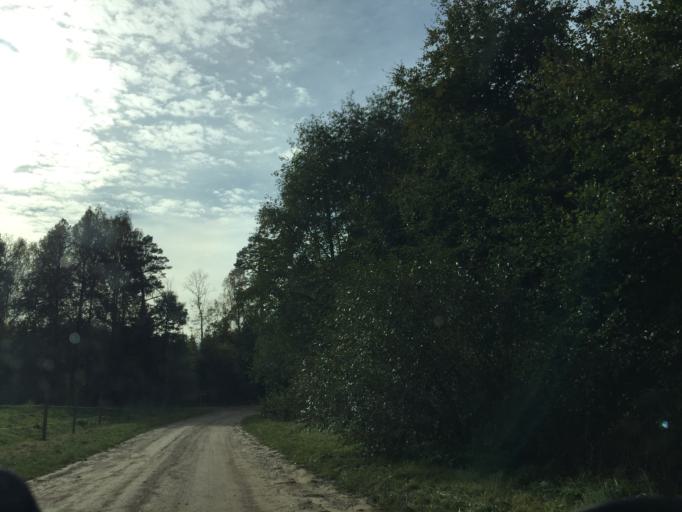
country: LV
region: Jaunpils
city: Jaunpils
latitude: 56.6103
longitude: 23.0102
